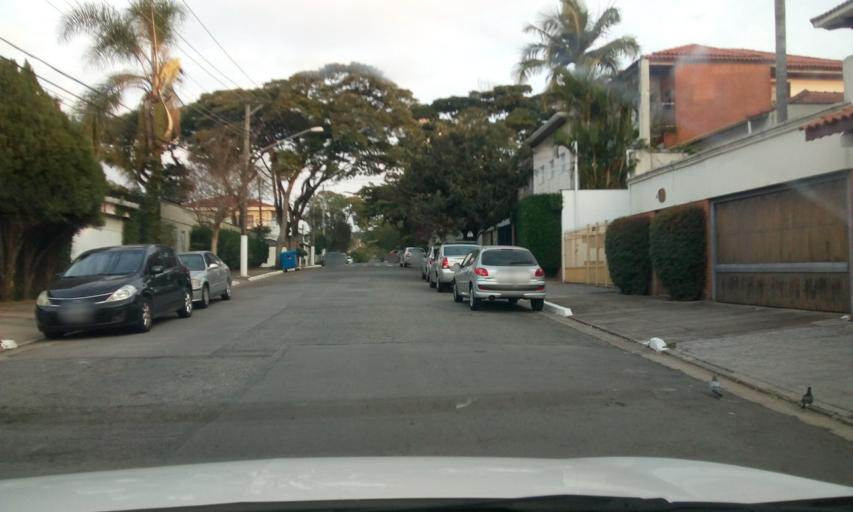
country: BR
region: Sao Paulo
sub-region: Sao Paulo
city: Sao Paulo
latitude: -23.6099
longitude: -46.6481
